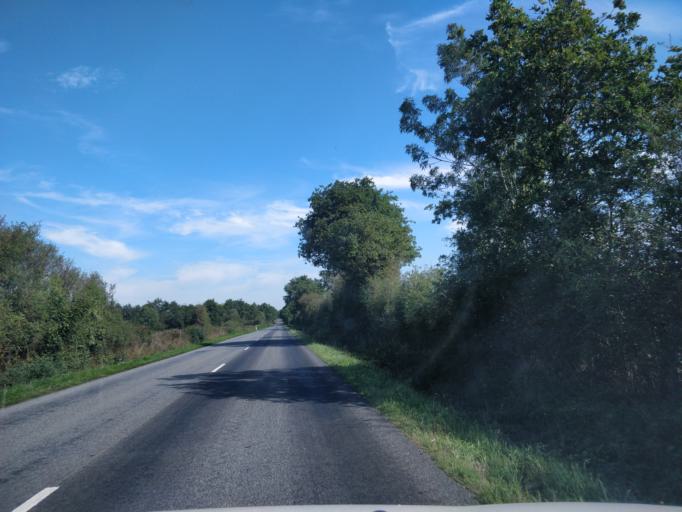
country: FR
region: Pays de la Loire
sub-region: Departement de la Loire-Atlantique
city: Campbon
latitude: 47.4176
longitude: -1.9305
